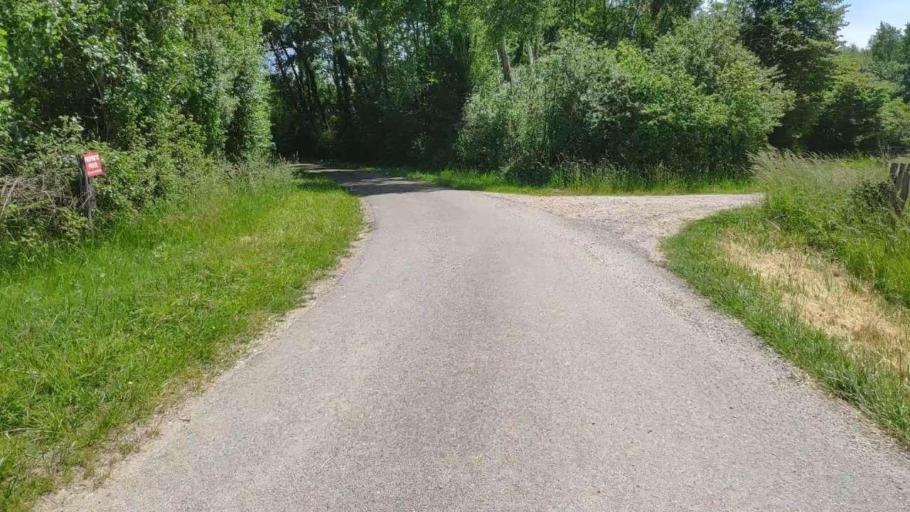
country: FR
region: Franche-Comte
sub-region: Departement du Jura
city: Bletterans
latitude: 46.7842
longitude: 5.4521
